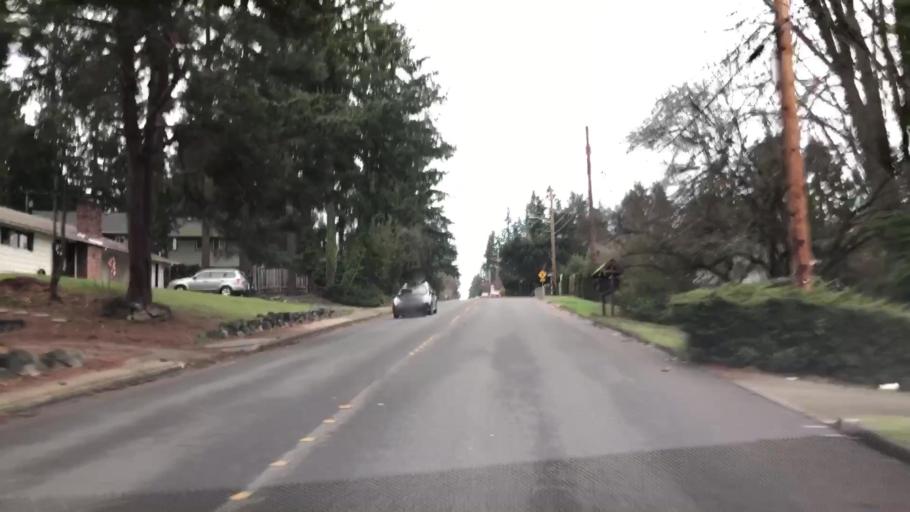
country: US
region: Washington
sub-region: King County
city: West Lake Sammamish
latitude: 47.6088
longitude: -122.1213
